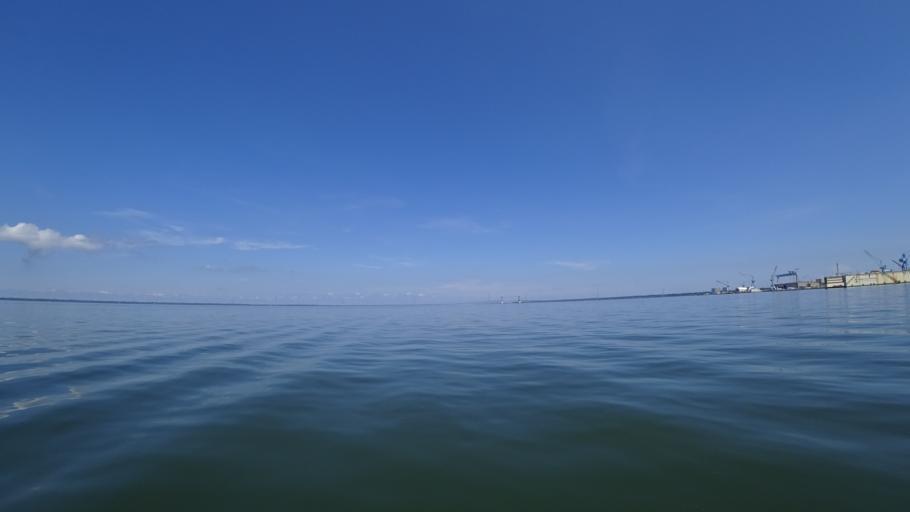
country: US
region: Virginia
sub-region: City of Newport News
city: Newport News
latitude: 36.9821
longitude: -76.4489
